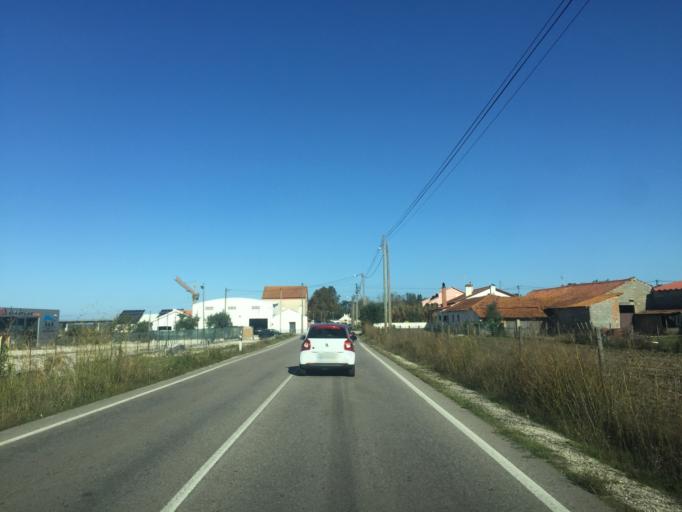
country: PT
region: Leiria
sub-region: Leiria
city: Amor
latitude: 39.8007
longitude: -8.8382
